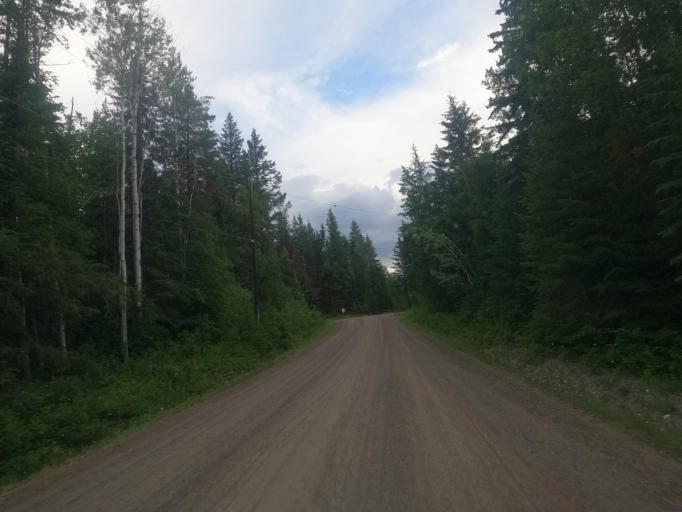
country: CA
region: British Columbia
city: Golden
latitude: 51.4534
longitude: -117.0037
